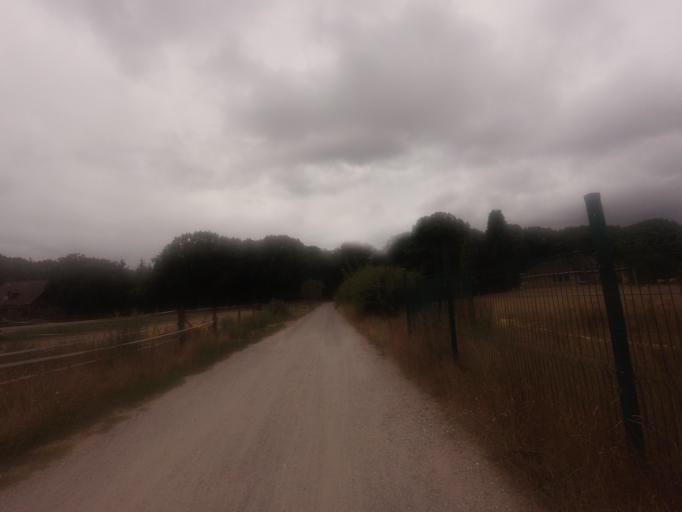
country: NL
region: Gelderland
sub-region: Gemeente Wijchen
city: Wijchen
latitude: 51.8014
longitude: 5.7621
